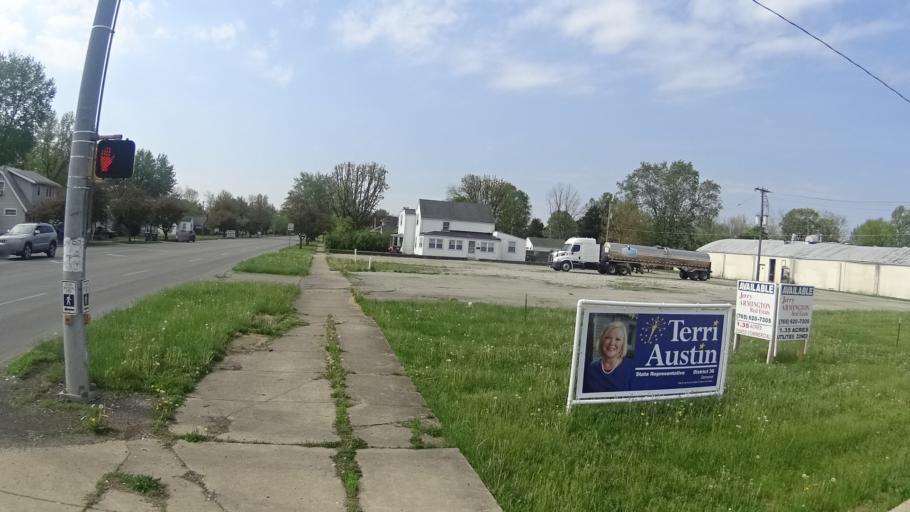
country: US
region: Indiana
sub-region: Madison County
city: Anderson
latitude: 40.1352
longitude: -85.6780
